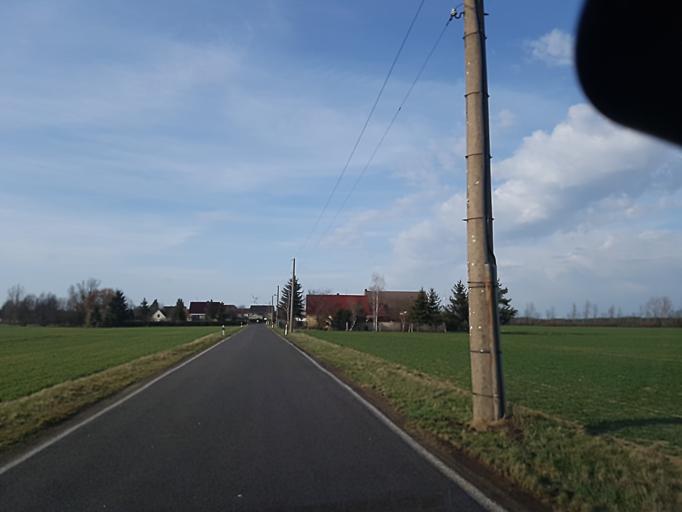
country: DE
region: Brandenburg
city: Falkenberg
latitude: 51.5447
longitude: 13.2946
